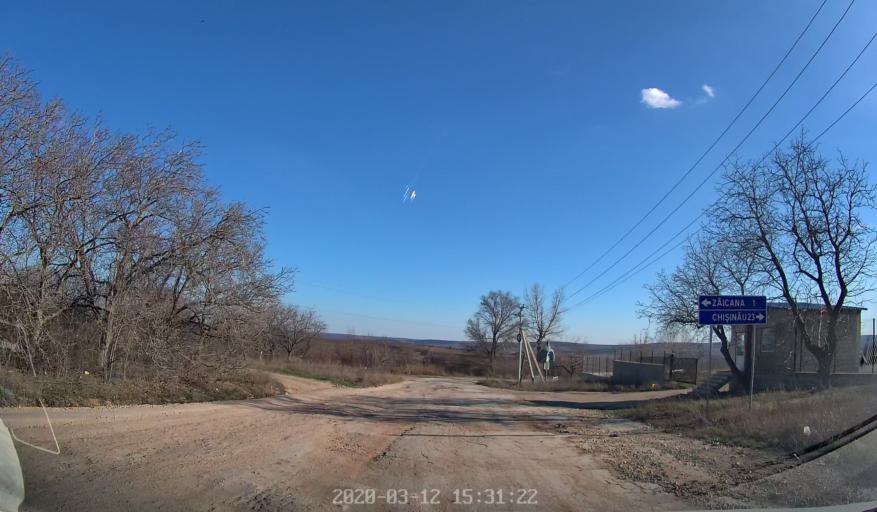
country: MD
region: Chisinau
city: Ciorescu
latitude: 47.1576
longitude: 28.9424
